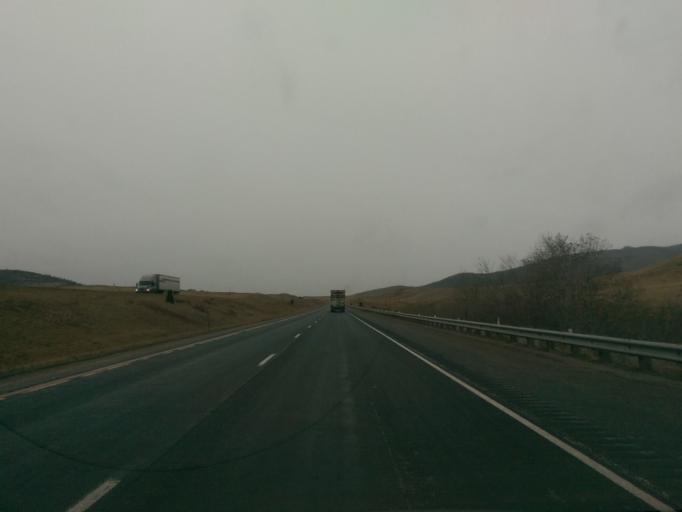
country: US
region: Montana
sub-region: Jefferson County
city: Whitehall
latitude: 45.8963
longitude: -111.8358
